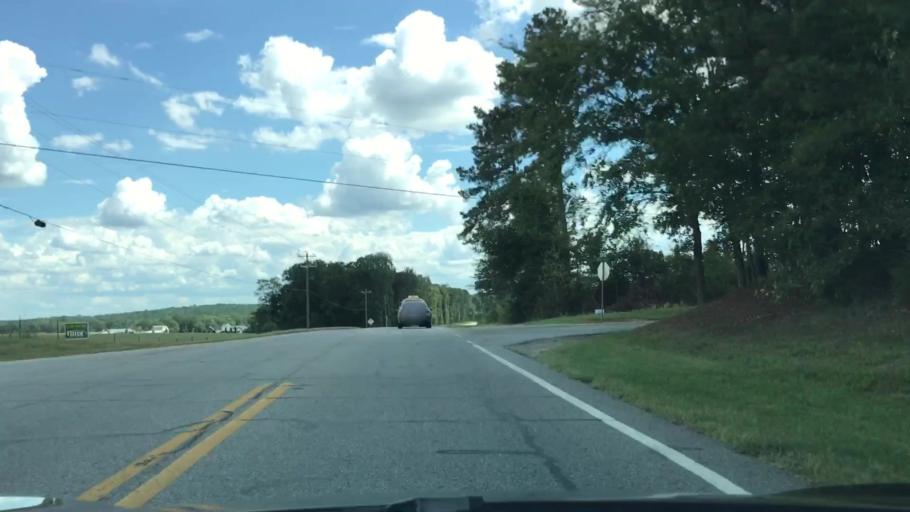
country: US
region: Georgia
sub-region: Oconee County
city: Watkinsville
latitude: 33.7912
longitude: -83.3226
